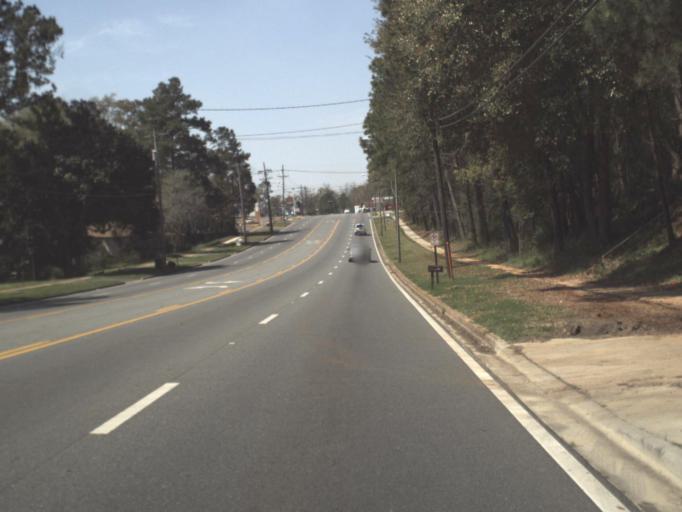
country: US
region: Florida
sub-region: Gadsden County
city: Quincy
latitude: 30.5847
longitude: -84.5654
